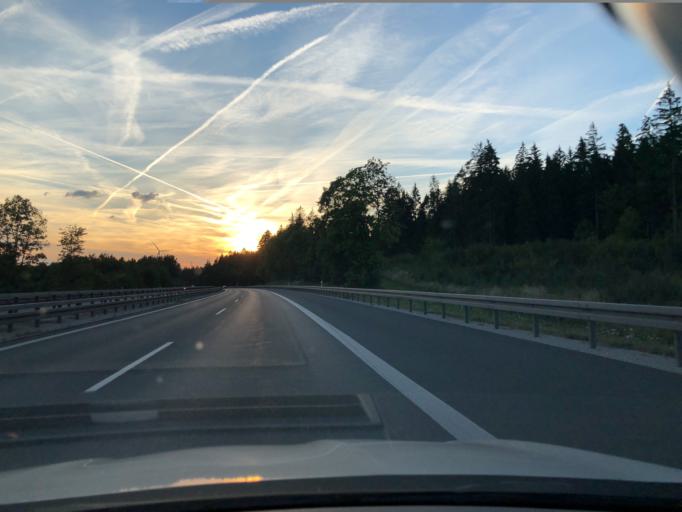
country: DE
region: Bavaria
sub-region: Regierungsbezirk Mittelfranken
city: Alfeld
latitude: 49.4172
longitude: 11.5010
